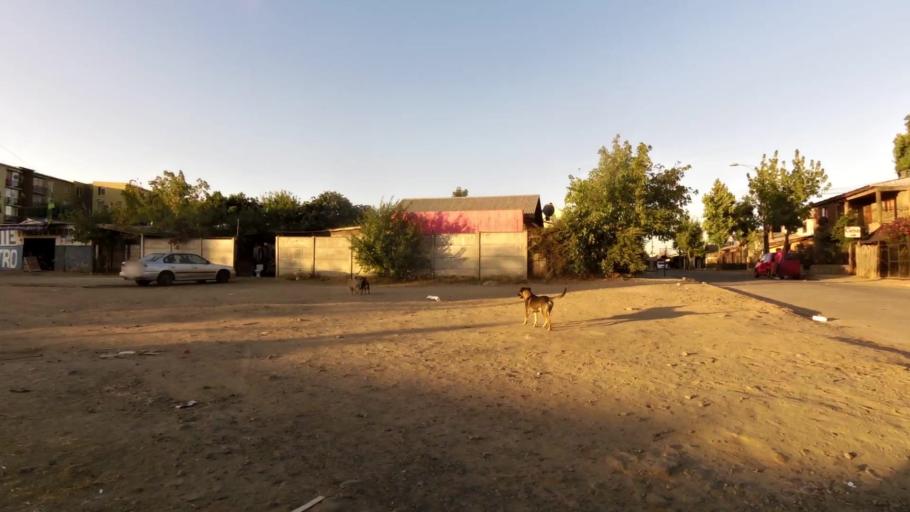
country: CL
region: Maule
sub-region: Provincia de Talca
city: Talca
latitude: -35.4442
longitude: -71.6385
